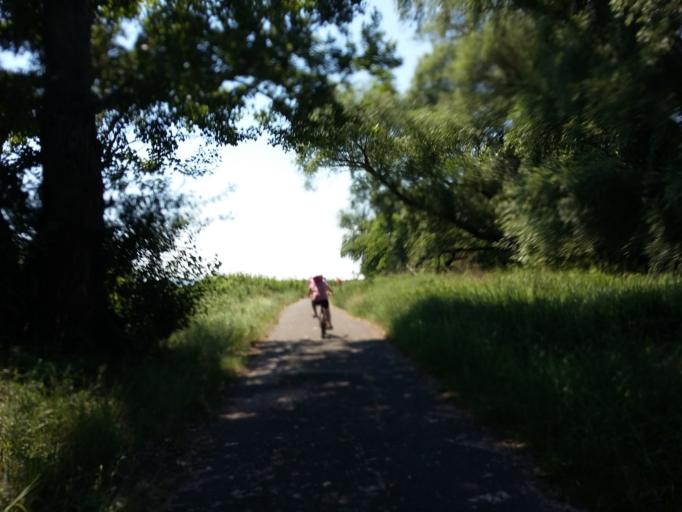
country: AT
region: Lower Austria
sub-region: Politischer Bezirk Ganserndorf
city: Marchegg
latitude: 48.2641
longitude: 16.9588
